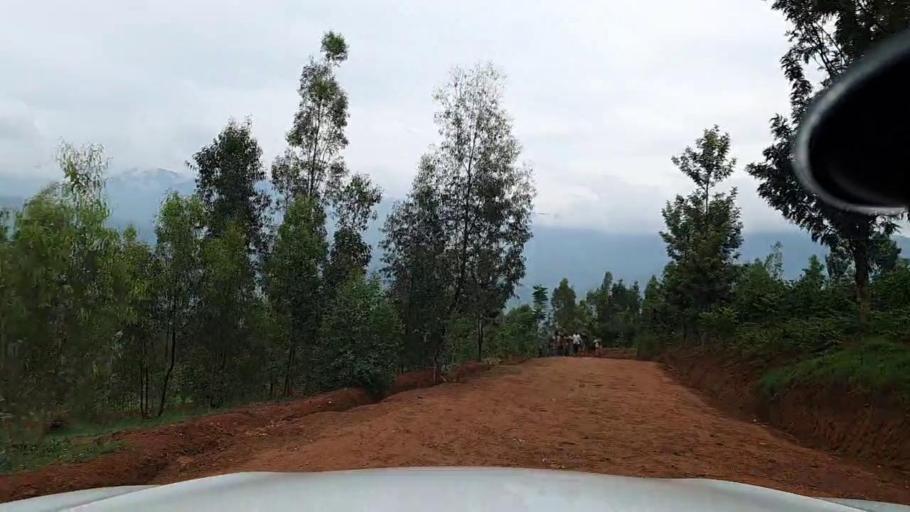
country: RW
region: Kigali
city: Kigali
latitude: -1.8782
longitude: 29.9138
